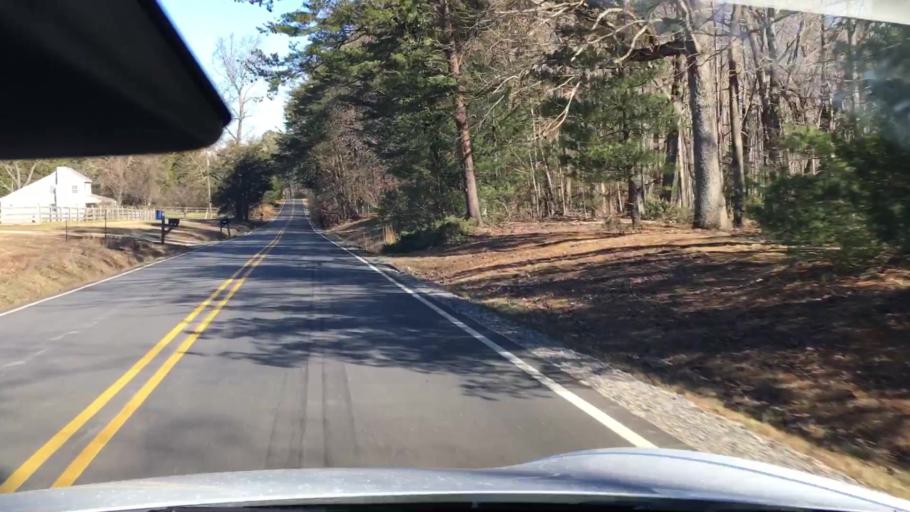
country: US
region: Virginia
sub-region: Powhatan County
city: Powhatan
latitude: 37.5749
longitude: -77.7742
